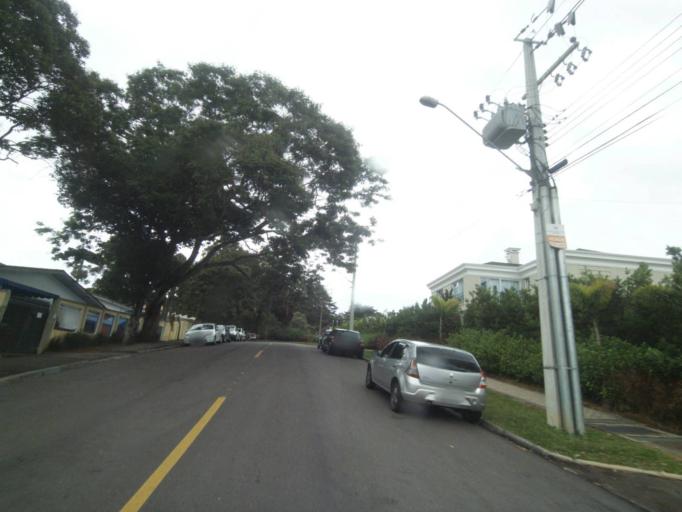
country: BR
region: Parana
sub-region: Curitiba
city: Curitiba
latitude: -25.4563
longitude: -49.3260
